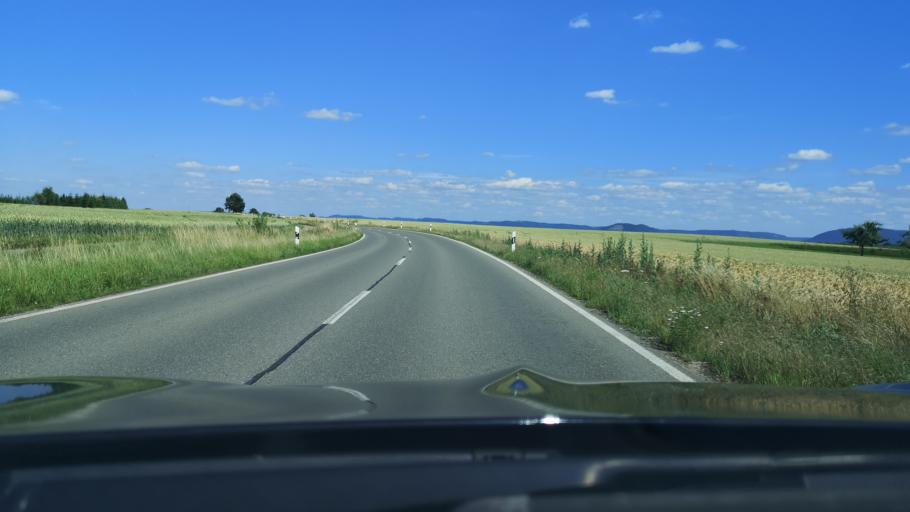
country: DE
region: Baden-Wuerttemberg
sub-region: Regierungsbezirk Stuttgart
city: Altenriet
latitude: 48.5917
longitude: 9.1986
